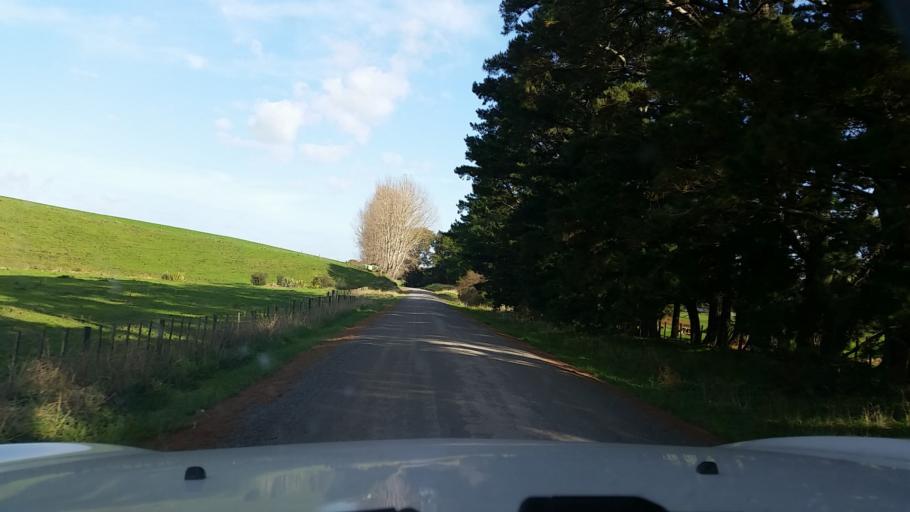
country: NZ
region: Bay of Plenty
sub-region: Western Bay of Plenty District
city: Katikati
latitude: -37.6105
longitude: 175.7964
